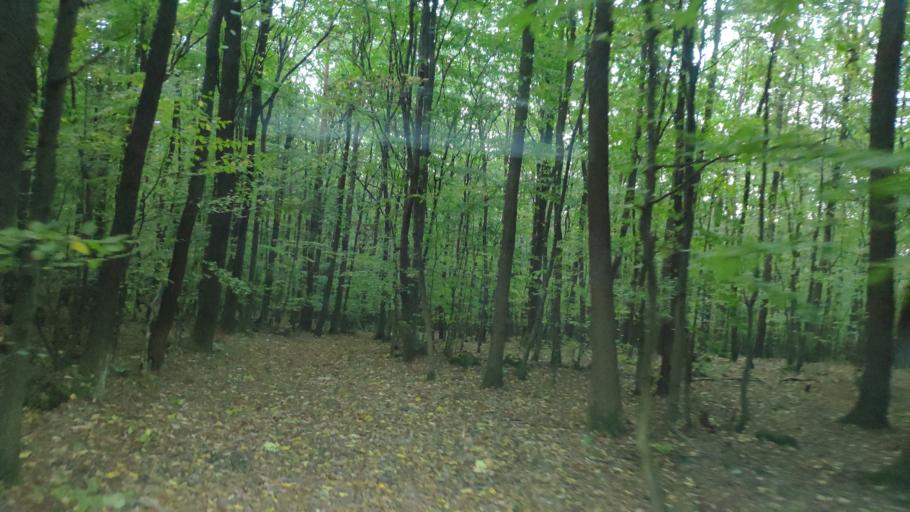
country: SK
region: Kosicky
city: Kosice
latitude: 48.6969
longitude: 21.1970
